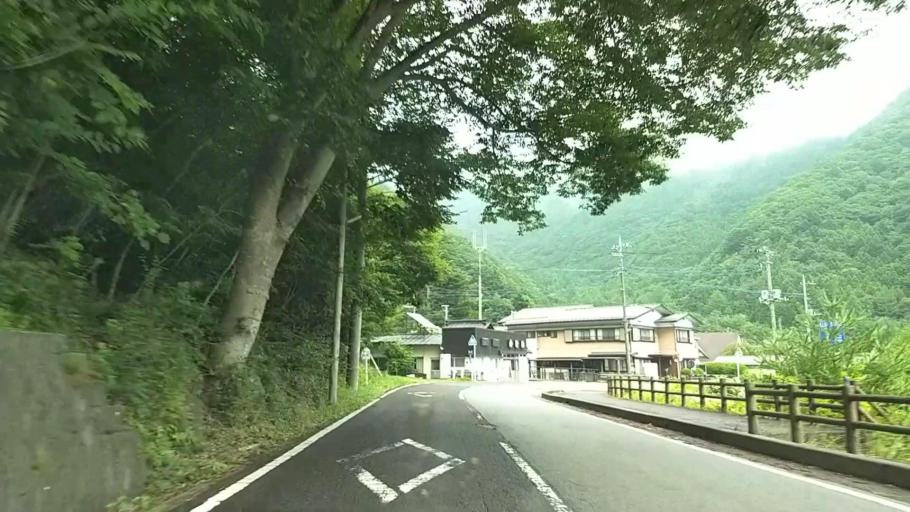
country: JP
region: Yamanashi
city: Fujikawaguchiko
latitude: 35.4943
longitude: 138.6086
